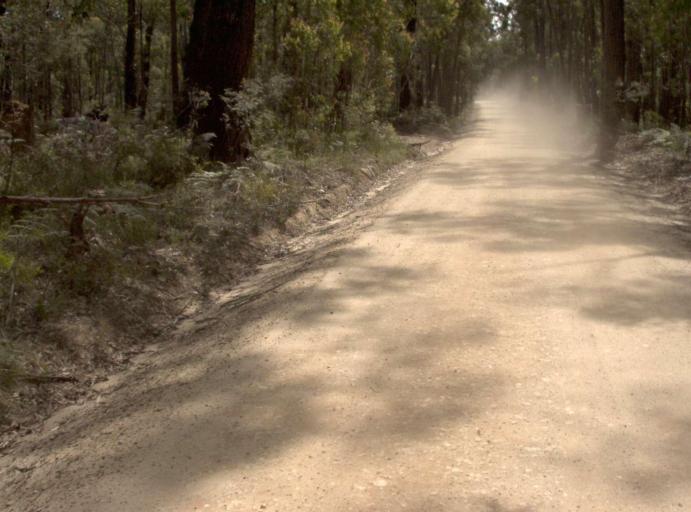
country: AU
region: Victoria
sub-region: East Gippsland
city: Lakes Entrance
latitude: -37.6569
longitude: 148.6447
